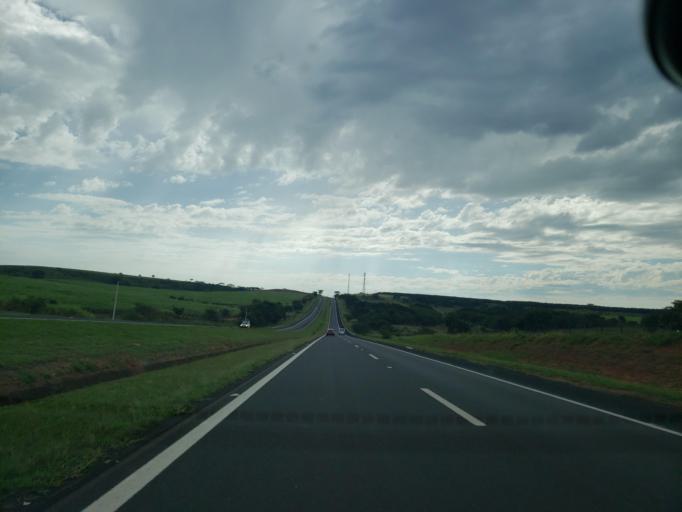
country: BR
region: Sao Paulo
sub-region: Cafelandia
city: Cafelandia
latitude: -21.7700
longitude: -49.6671
